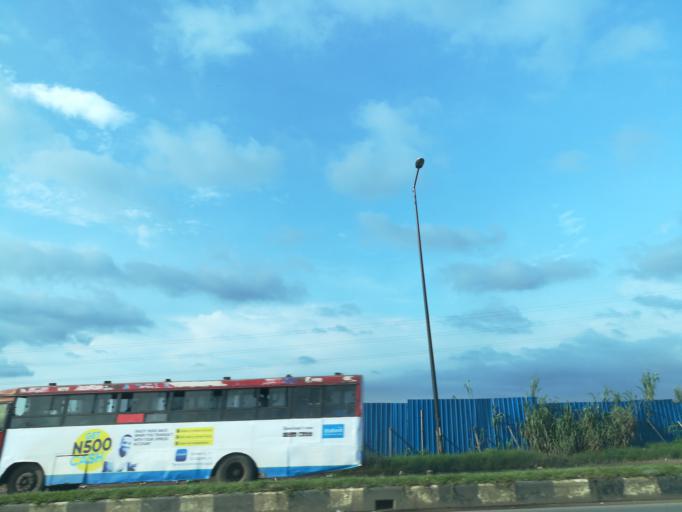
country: NG
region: Lagos
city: Ebute Ikorodu
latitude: 6.6188
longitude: 3.4599
